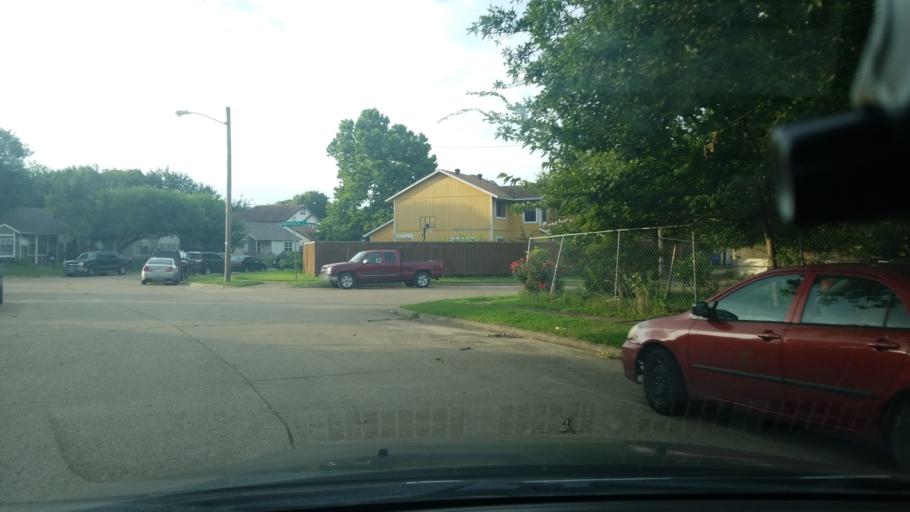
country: US
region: Texas
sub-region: Dallas County
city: Balch Springs
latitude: 32.7478
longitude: -96.6453
